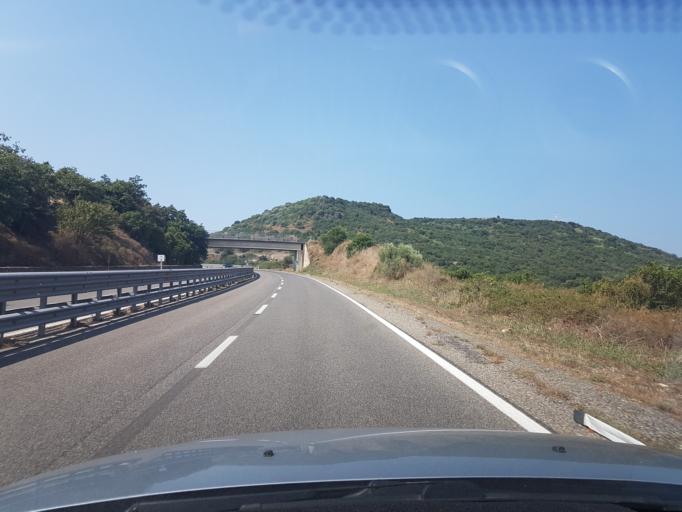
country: IT
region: Sardinia
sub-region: Provincia di Oristano
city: Soddi
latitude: 40.1440
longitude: 8.8749
